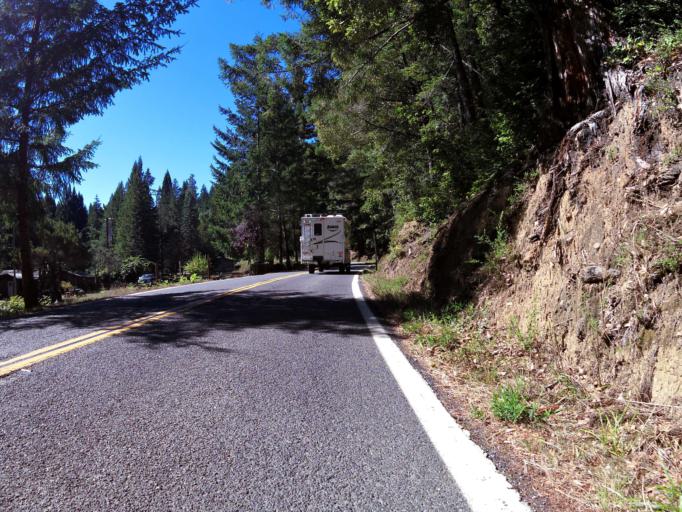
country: US
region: California
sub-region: Humboldt County
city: Redway
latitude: 39.8157
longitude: -123.7851
